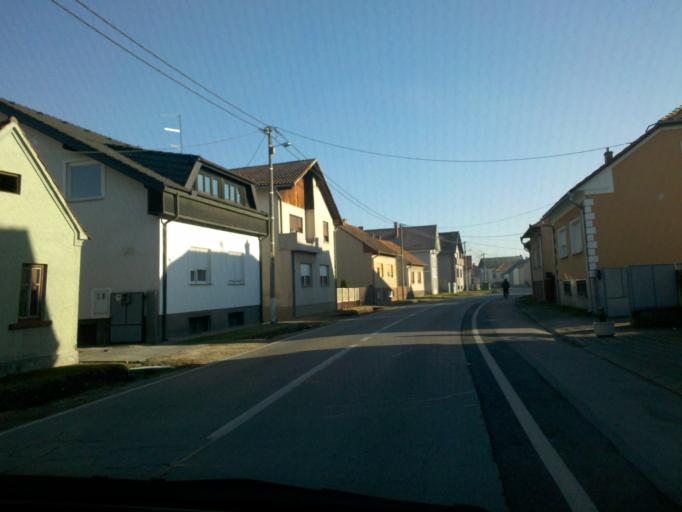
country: HR
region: Medimurska
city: Mala Subotica
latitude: 46.3785
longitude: 16.5355
